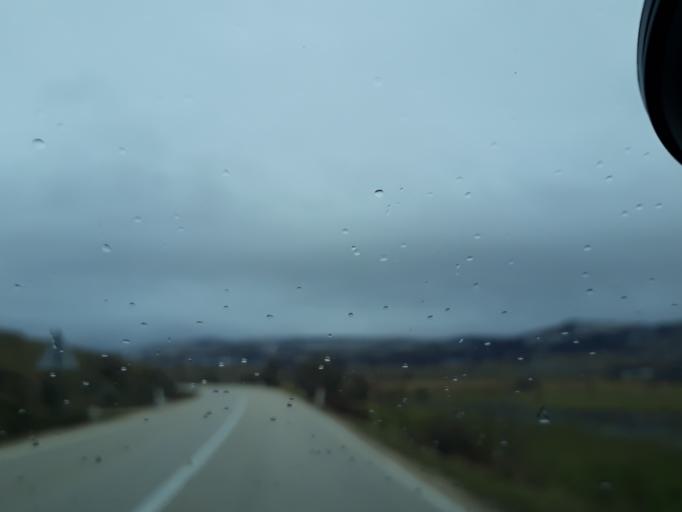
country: BA
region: Federation of Bosnia and Herzegovina
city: Tomislavgrad
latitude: 43.8340
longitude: 17.1875
